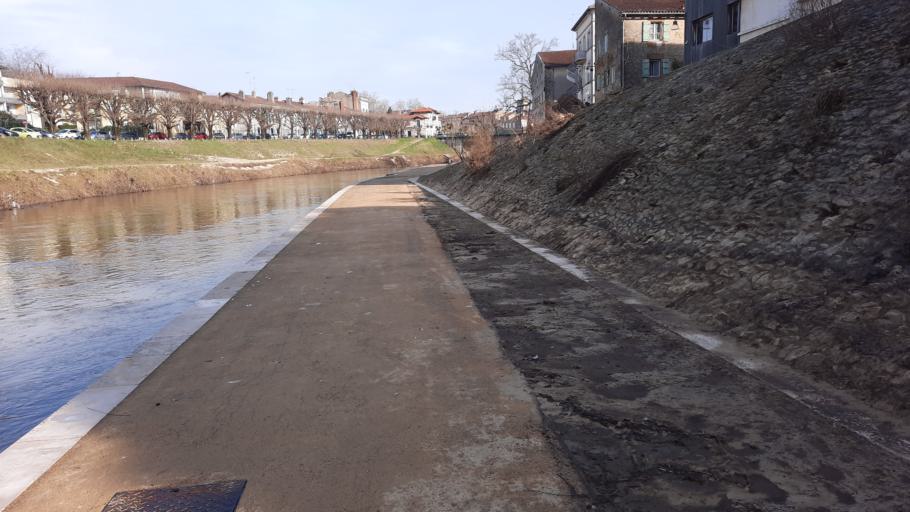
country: FR
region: Aquitaine
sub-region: Departement des Landes
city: Mont-de-Marsan
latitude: 43.8892
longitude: -0.5054
